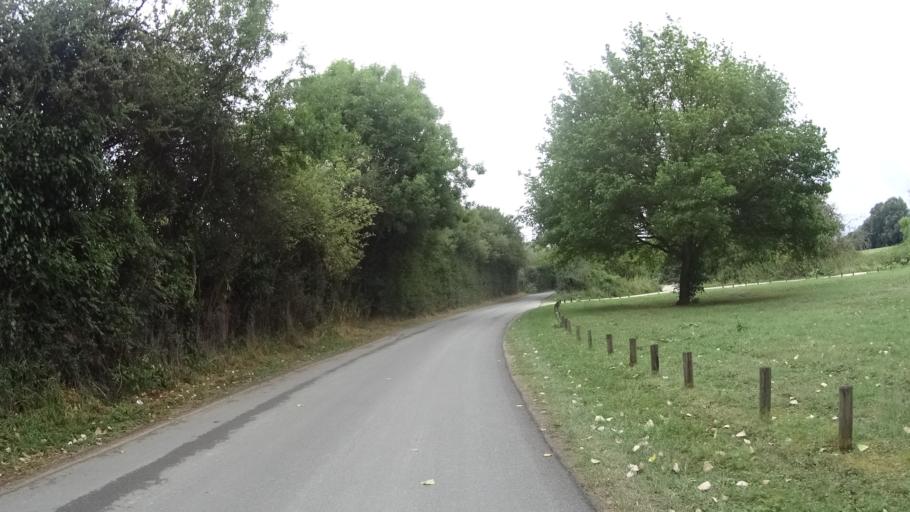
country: FR
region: Centre
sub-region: Departement du Loiret
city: Beaugency
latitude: 47.7858
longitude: 1.6473
